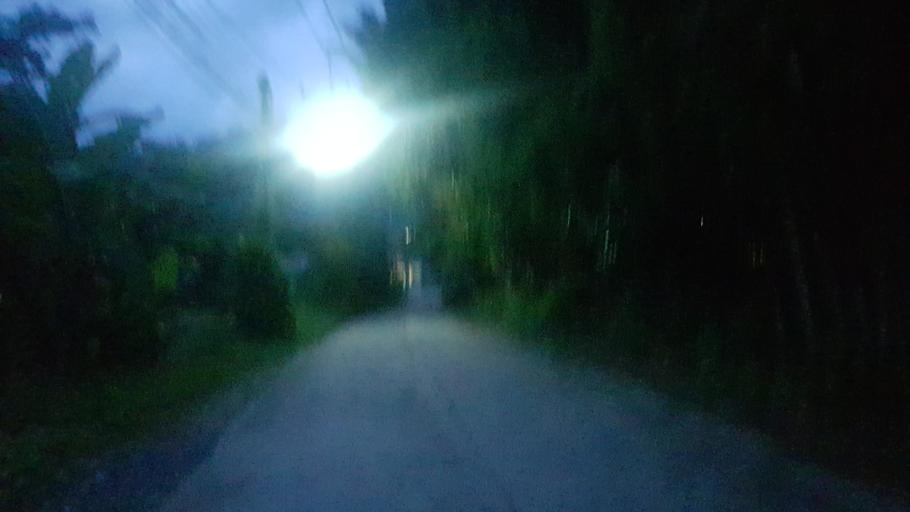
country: TH
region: Phangnga
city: Takua Pa
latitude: 8.9128
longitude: 98.5267
